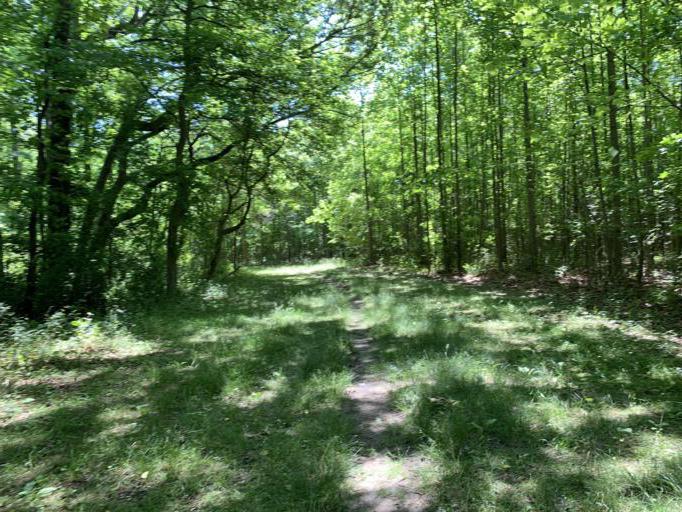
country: US
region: Delaware
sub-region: Kent County
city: Clayton
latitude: 39.3339
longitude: -75.6668
